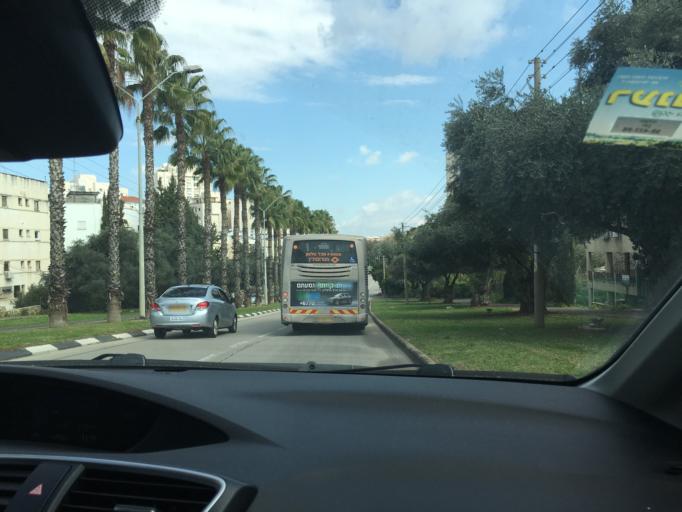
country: IL
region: Tel Aviv
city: Ramat HaSharon
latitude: 32.1493
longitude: 34.8405
